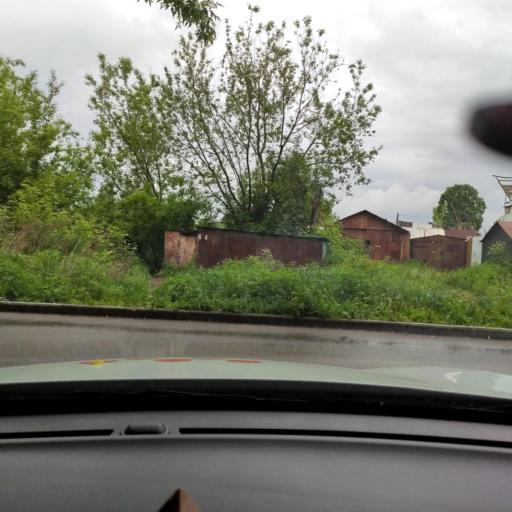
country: RU
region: Tatarstan
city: Staroye Arakchino
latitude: 55.8792
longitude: 49.0181
